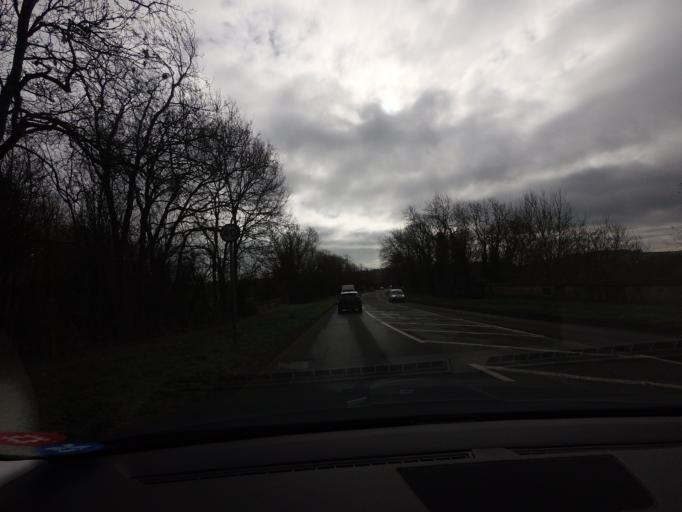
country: GB
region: England
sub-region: Kent
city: Eynsford
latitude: 51.3828
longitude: 0.2236
